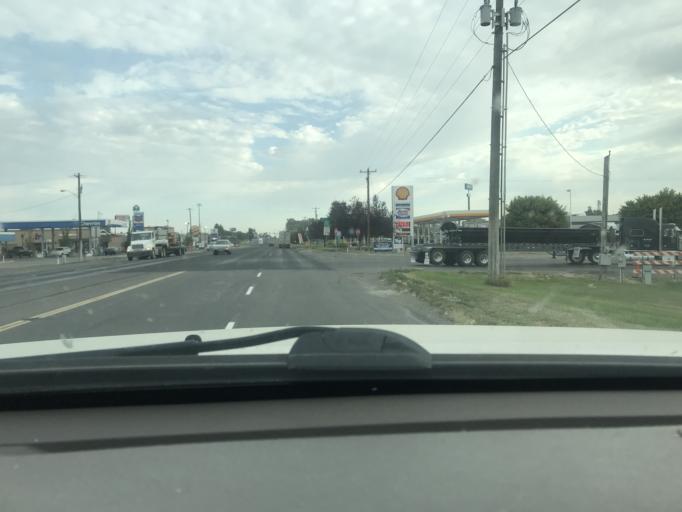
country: US
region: Idaho
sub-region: Jerome County
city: Jerome
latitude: 42.6907
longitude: -114.5184
